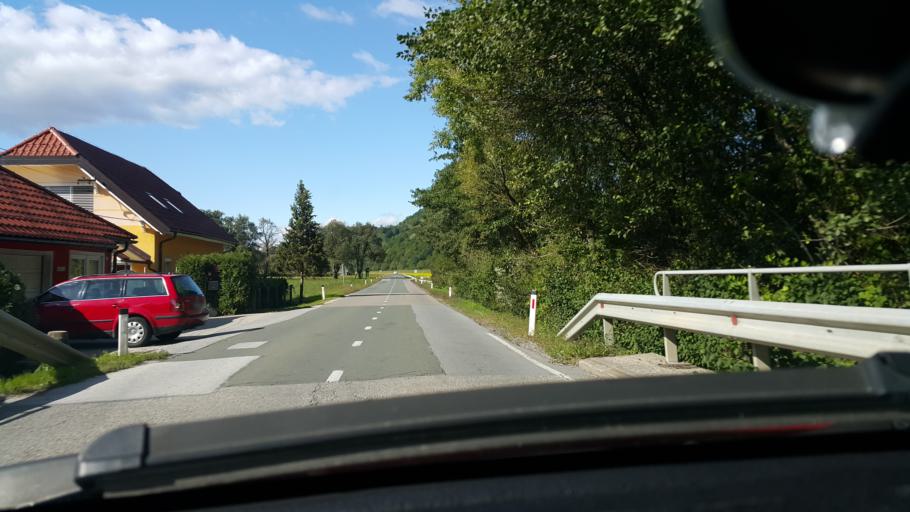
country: SI
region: Kungota
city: Zgornja Kungota
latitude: 46.6216
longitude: 15.6338
